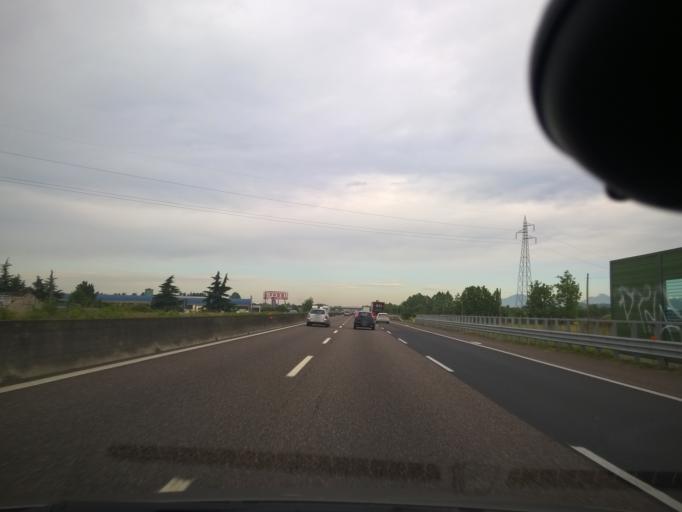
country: IT
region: Lombardy
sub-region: Provincia di Bergamo
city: Bolgare
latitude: 45.6401
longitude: 9.8234
